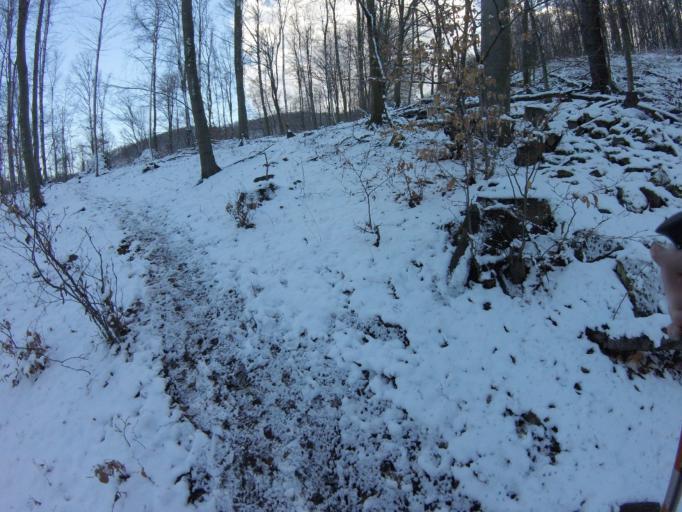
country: HU
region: Pest
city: Pilisszentkereszt
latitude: 47.7267
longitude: 18.8961
